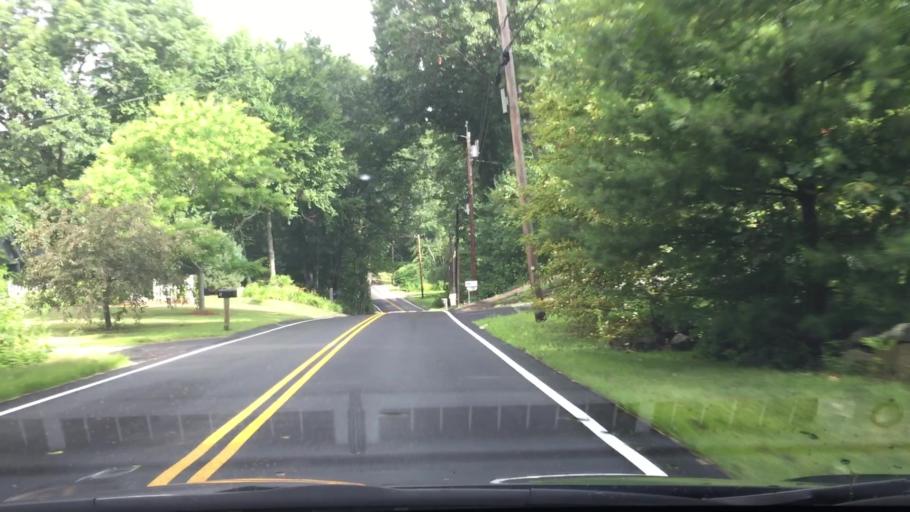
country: US
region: Massachusetts
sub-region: Middlesex County
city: Littleton Common
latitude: 42.5208
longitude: -71.4576
